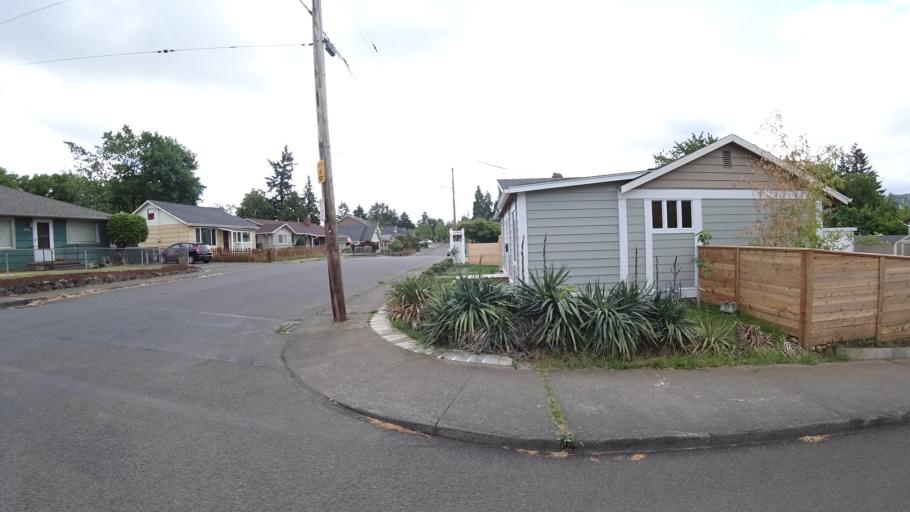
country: US
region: Oregon
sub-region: Multnomah County
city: Lents
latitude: 45.4833
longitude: -122.5595
